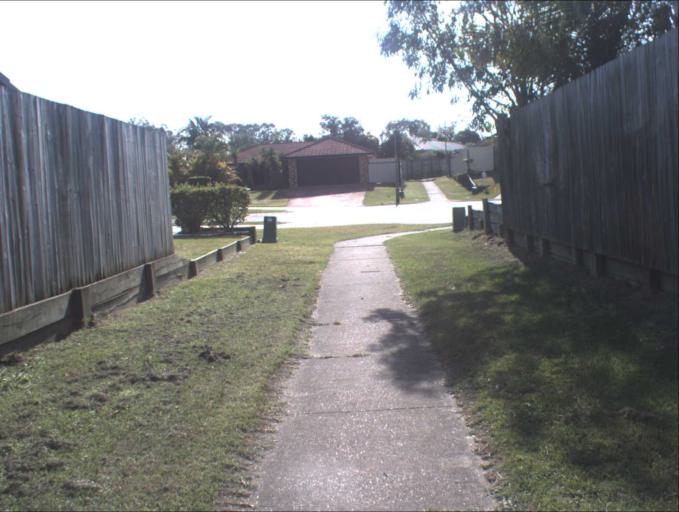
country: AU
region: Queensland
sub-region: Logan
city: Park Ridge South
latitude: -27.6798
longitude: 153.0568
